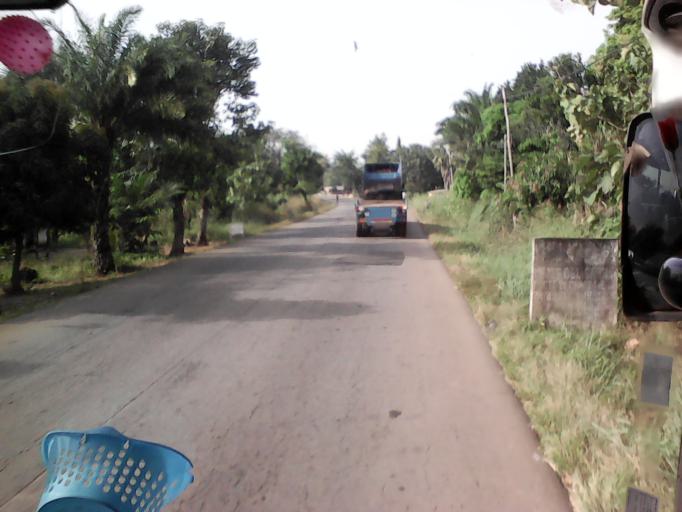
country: TG
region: Kara
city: Kara
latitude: 9.4529
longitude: 1.2138
